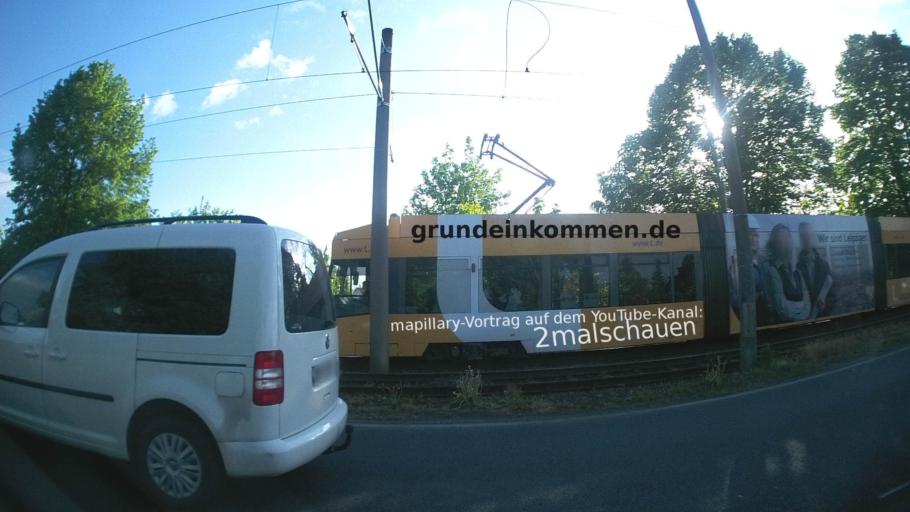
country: DE
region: Saxony
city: Markkleeberg
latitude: 51.2982
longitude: 12.4343
